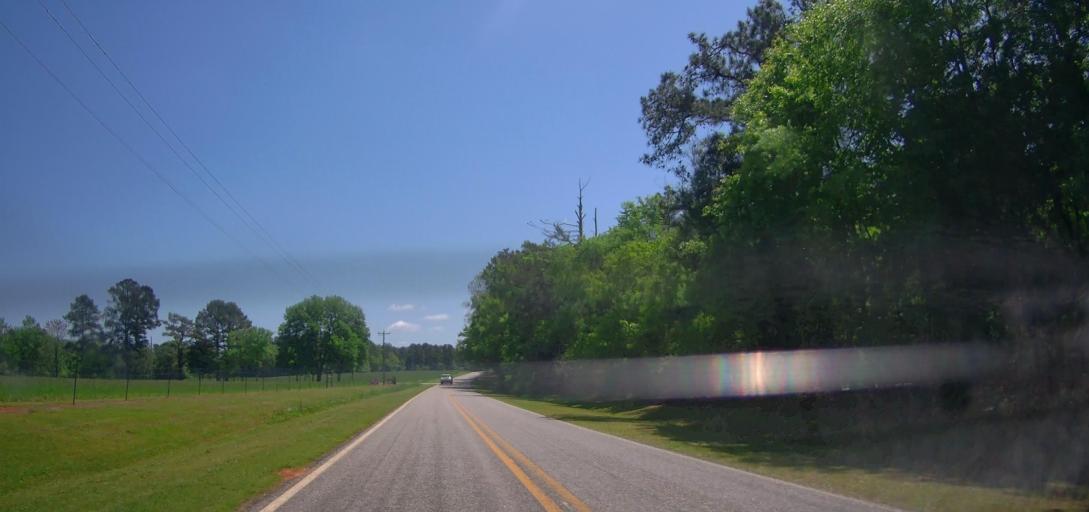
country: US
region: Georgia
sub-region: Jasper County
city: Monticello
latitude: 33.2773
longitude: -83.6677
